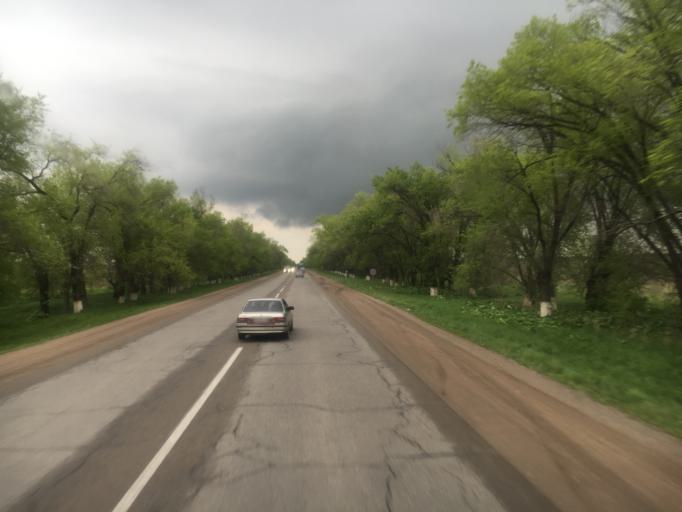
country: KZ
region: Almaty Oblysy
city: Burunday
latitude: 43.2539
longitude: 76.6683
